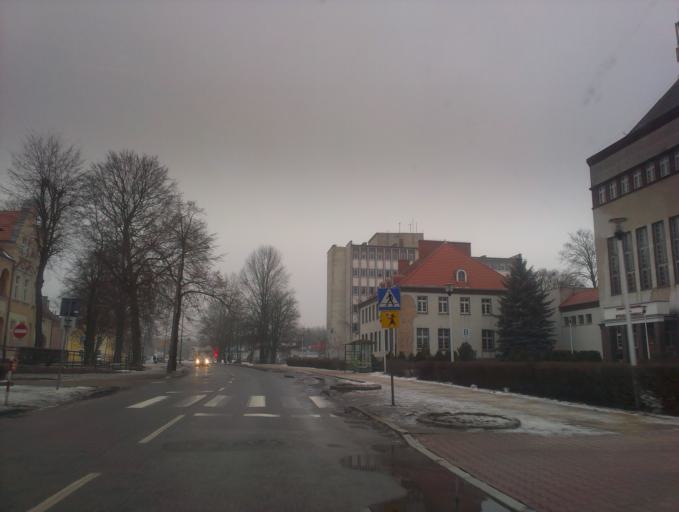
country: PL
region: Greater Poland Voivodeship
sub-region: Powiat pilski
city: Pila
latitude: 53.1562
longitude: 16.7375
